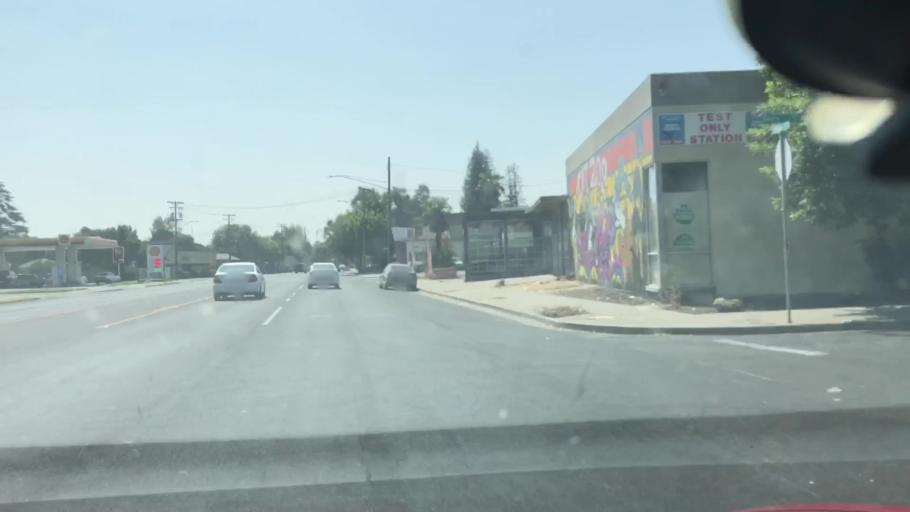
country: US
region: California
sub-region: San Joaquin County
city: Stockton
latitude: 37.9748
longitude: -121.2973
